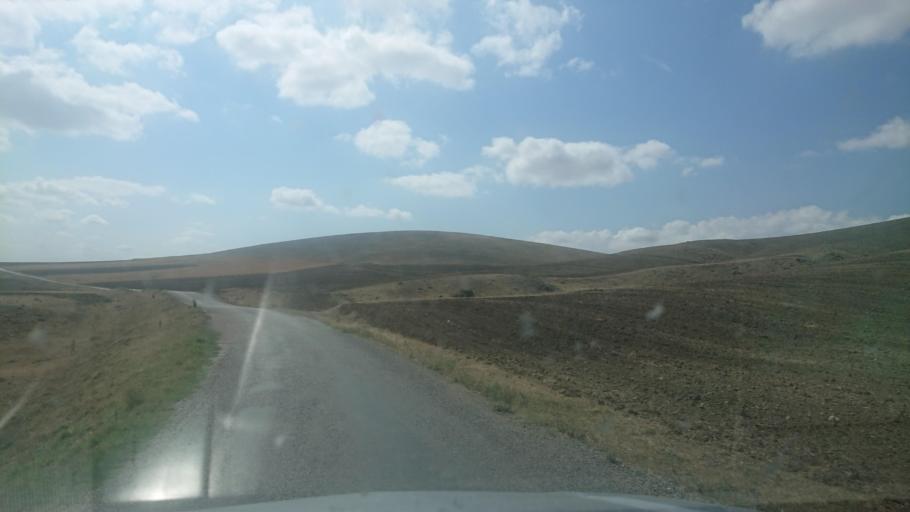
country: TR
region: Aksaray
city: Sariyahsi
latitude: 39.0037
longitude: 33.9617
